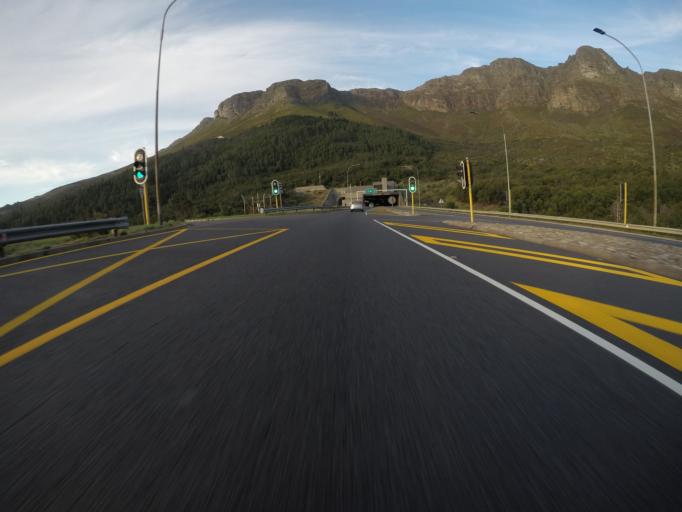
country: ZA
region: Western Cape
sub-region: Cape Winelands District Municipality
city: Paarl
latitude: -33.7357
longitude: 19.0701
